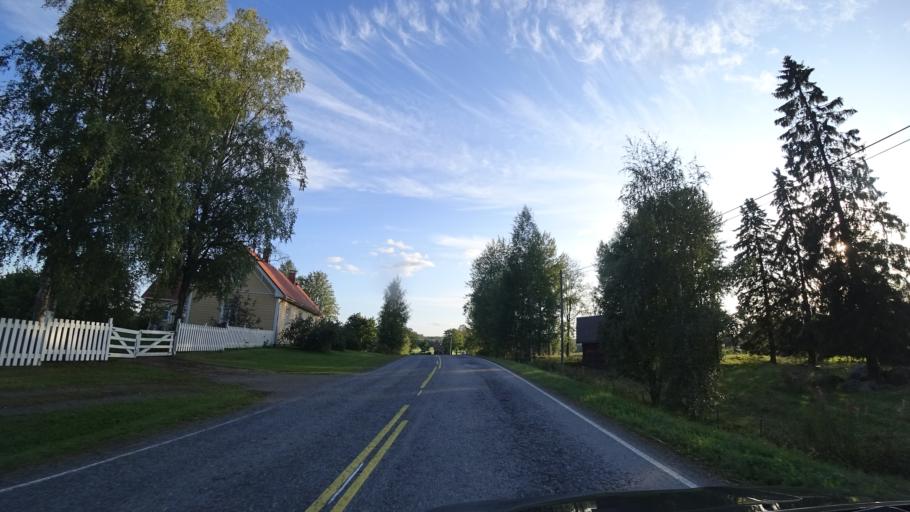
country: FI
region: Haeme
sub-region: Haemeenlinna
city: Lammi
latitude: 61.0448
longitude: 24.9402
